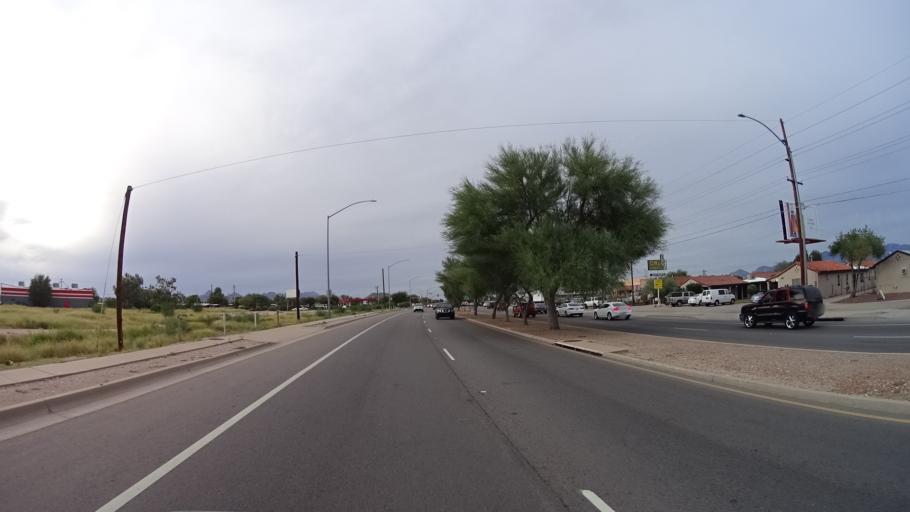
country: US
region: Arizona
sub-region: Pima County
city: South Tucson
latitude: 32.1671
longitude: -110.9417
